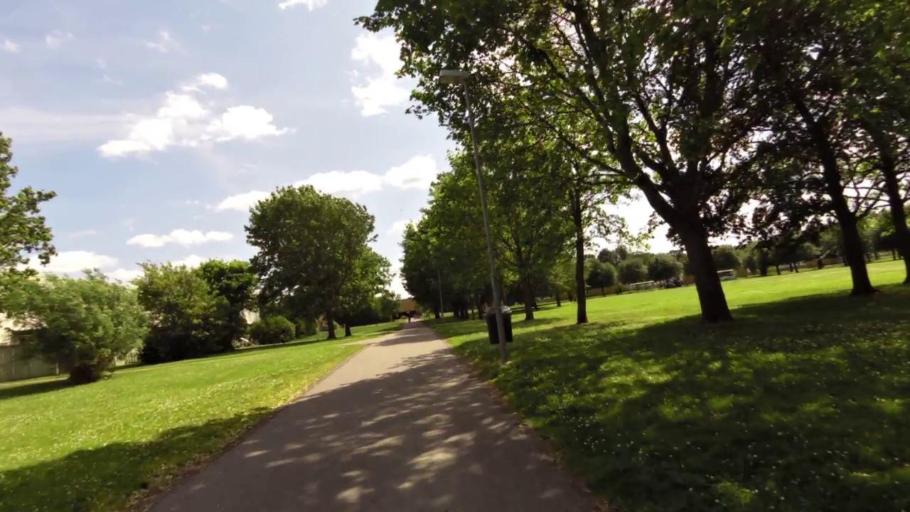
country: SE
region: OEstergoetland
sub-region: Linkopings Kommun
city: Linkoping
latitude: 58.4291
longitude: 15.5784
